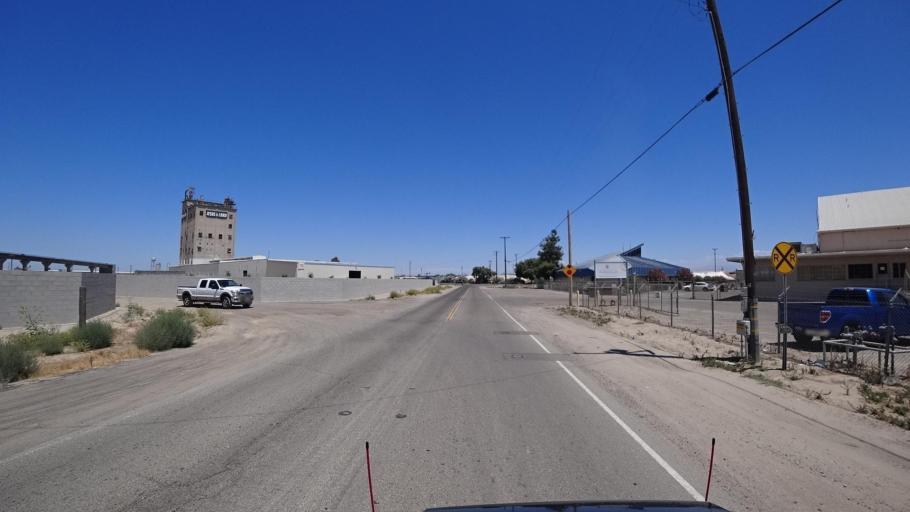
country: US
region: California
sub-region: Fresno County
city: Fresno
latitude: 36.6947
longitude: -119.7547
